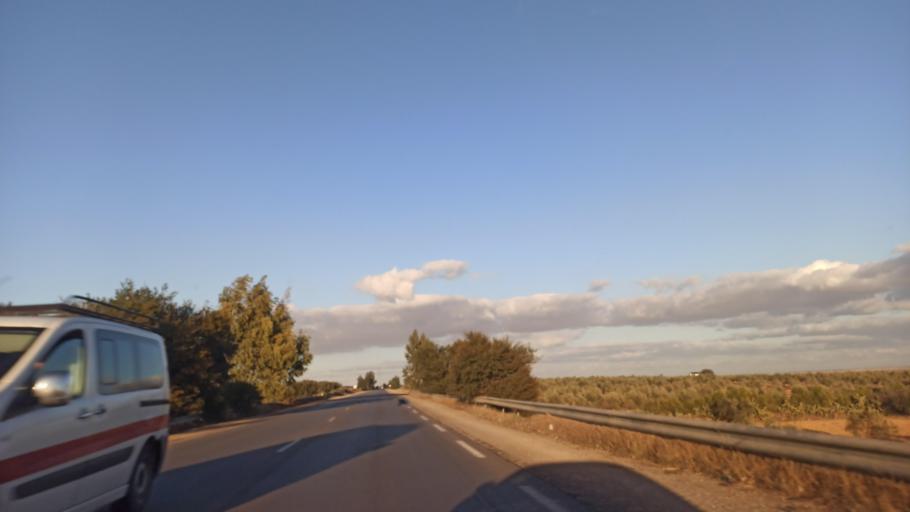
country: TN
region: Al Qayrawan
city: Sbikha
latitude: 35.8691
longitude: 10.2150
